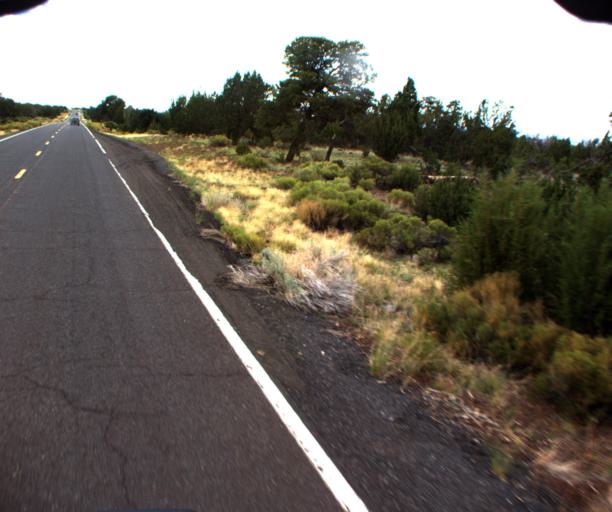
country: US
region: Arizona
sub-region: Coconino County
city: Parks
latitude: 35.5470
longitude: -111.8600
